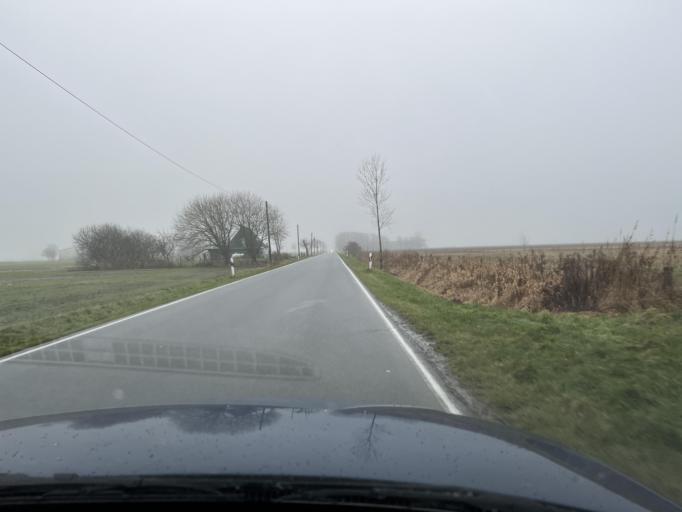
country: DE
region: Schleswig-Holstein
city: Wesselburenerkoog
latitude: 54.2530
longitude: 8.9040
